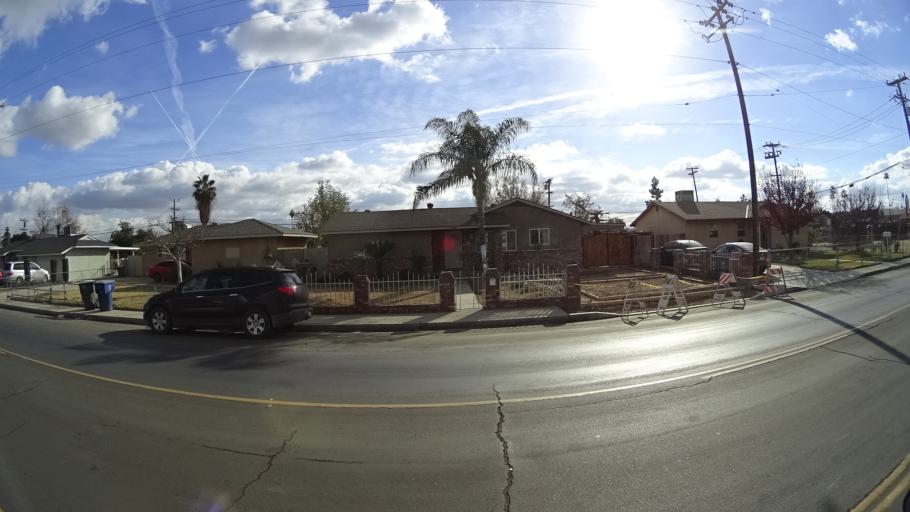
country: US
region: California
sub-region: Kern County
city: Bakersfield
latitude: 35.3322
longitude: -119.0202
